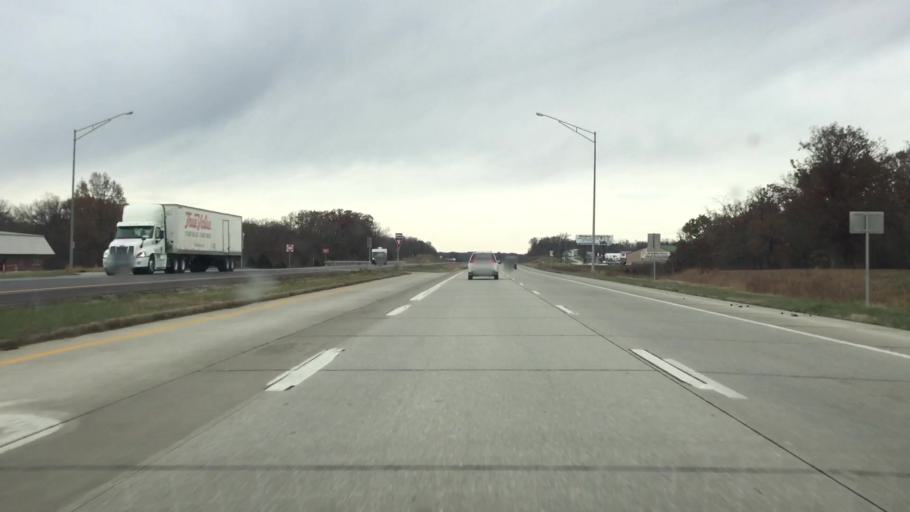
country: US
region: Missouri
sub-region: Saint Clair County
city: Osceola
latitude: 38.0752
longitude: -93.7012
